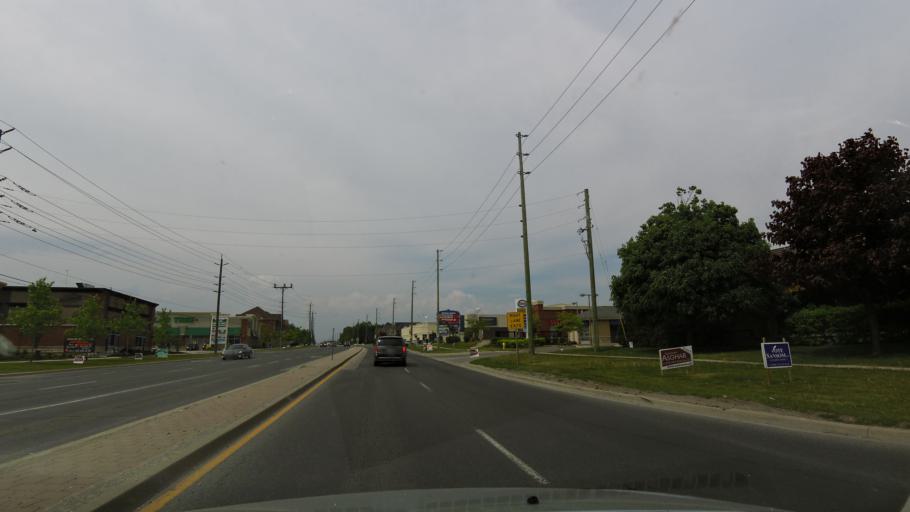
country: CA
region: Ontario
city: Oshawa
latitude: 43.9220
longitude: -78.9279
